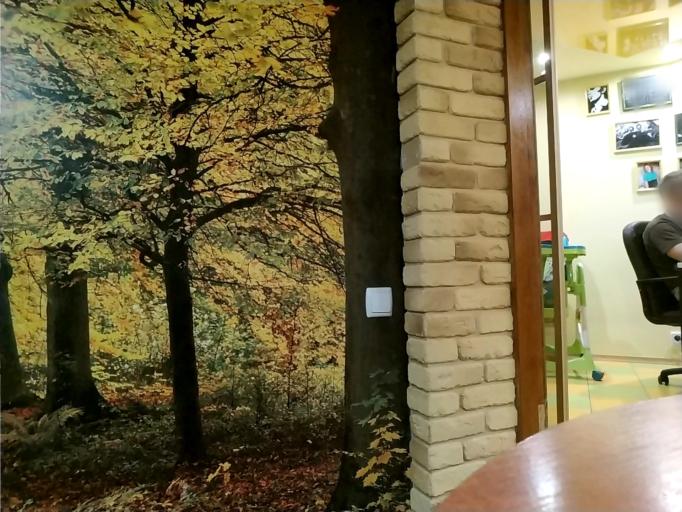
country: RU
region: Tverskaya
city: Zapadnaya Dvina
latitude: 56.3198
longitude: 31.9291
